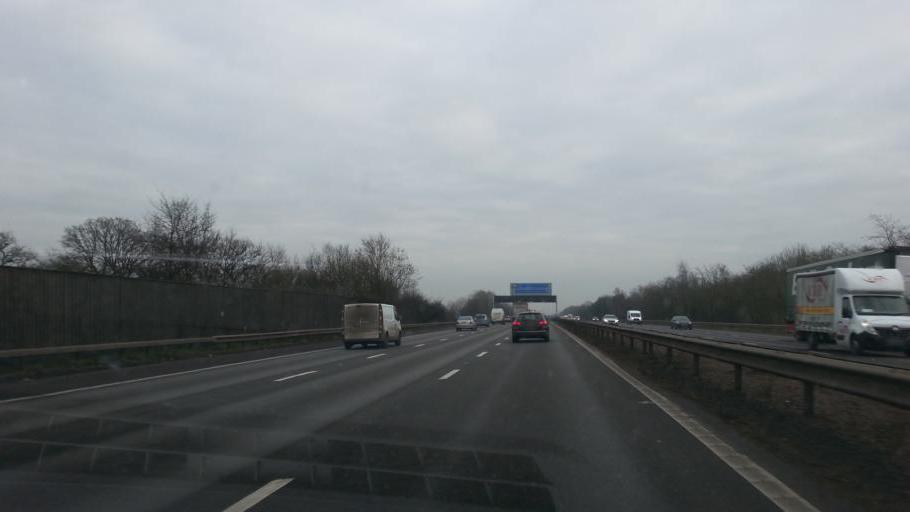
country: GB
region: England
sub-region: Warwickshire
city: Exhall
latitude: 52.4488
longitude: -1.4620
